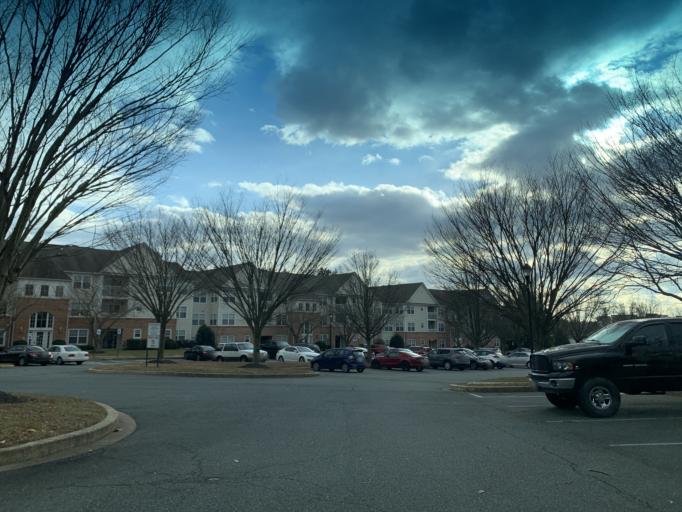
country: US
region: Maryland
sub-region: Harford County
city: South Bel Air
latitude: 39.5391
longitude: -76.3183
